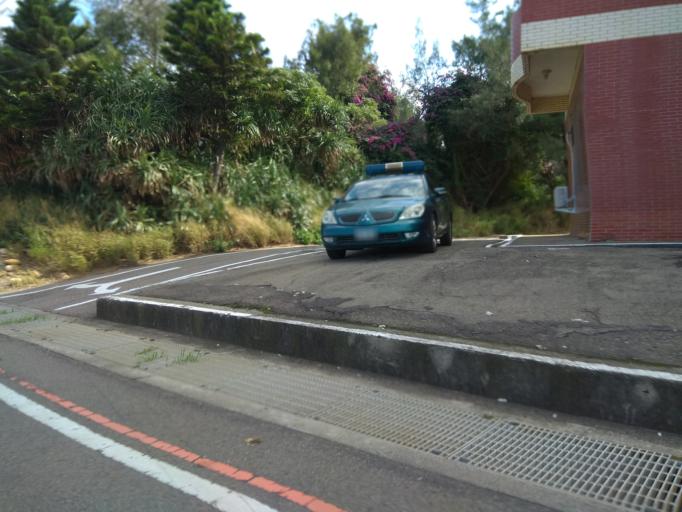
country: TW
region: Taiwan
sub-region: Hsinchu
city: Zhubei
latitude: 24.9894
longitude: 121.0163
